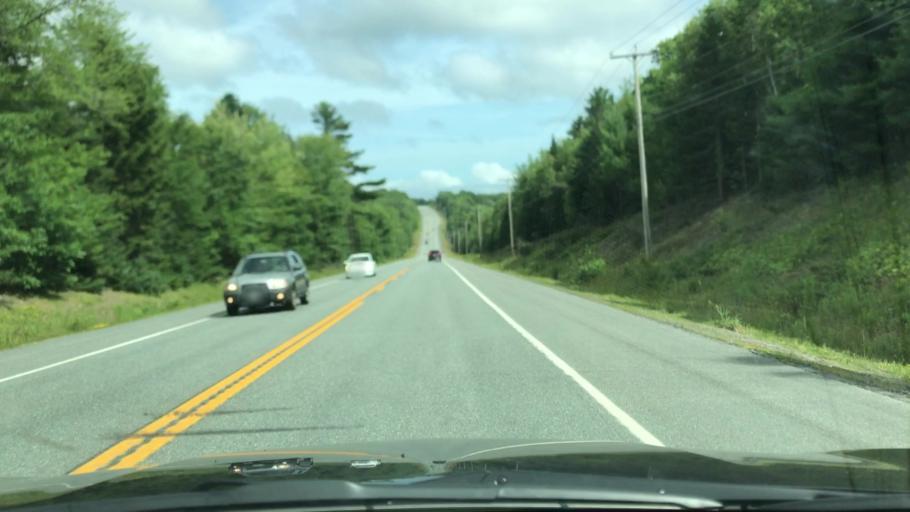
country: US
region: Maine
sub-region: Hancock County
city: Surry
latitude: 44.5517
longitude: -68.5330
